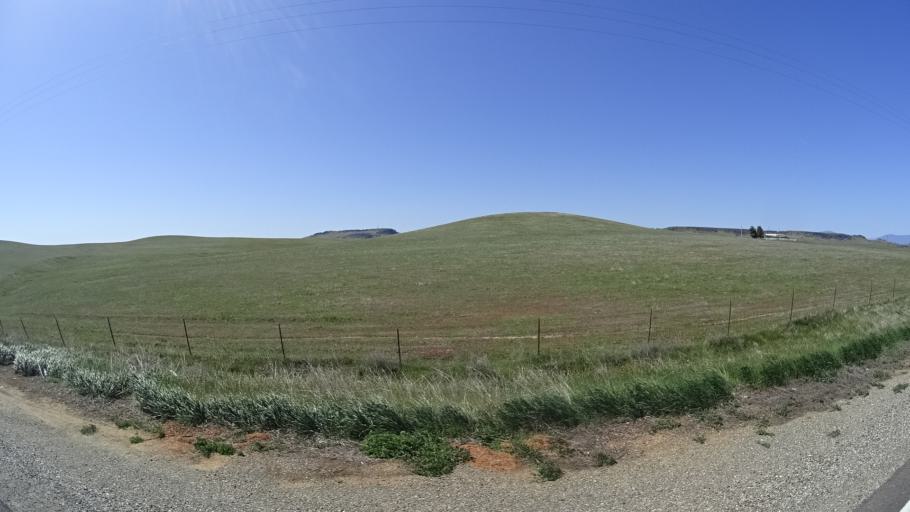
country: US
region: California
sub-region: Glenn County
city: Orland
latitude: 39.7856
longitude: -122.3003
